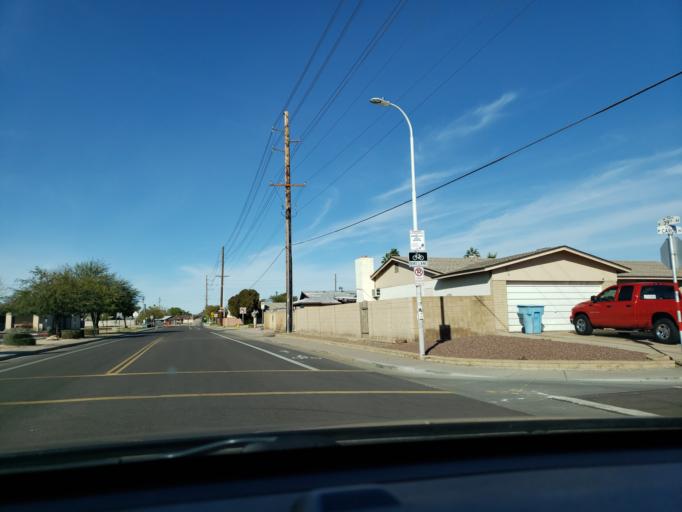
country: US
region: Arizona
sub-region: Maricopa County
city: Glendale
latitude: 33.5728
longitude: -112.1429
